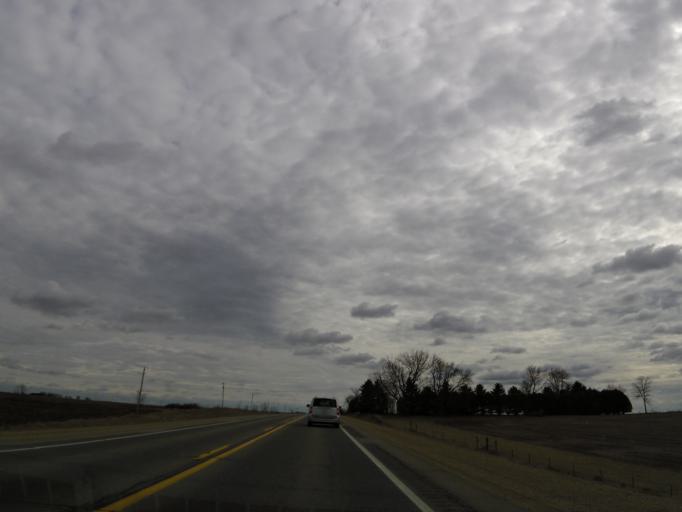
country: US
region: Iowa
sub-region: Chickasaw County
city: New Hampton
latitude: 43.1603
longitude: -92.2989
